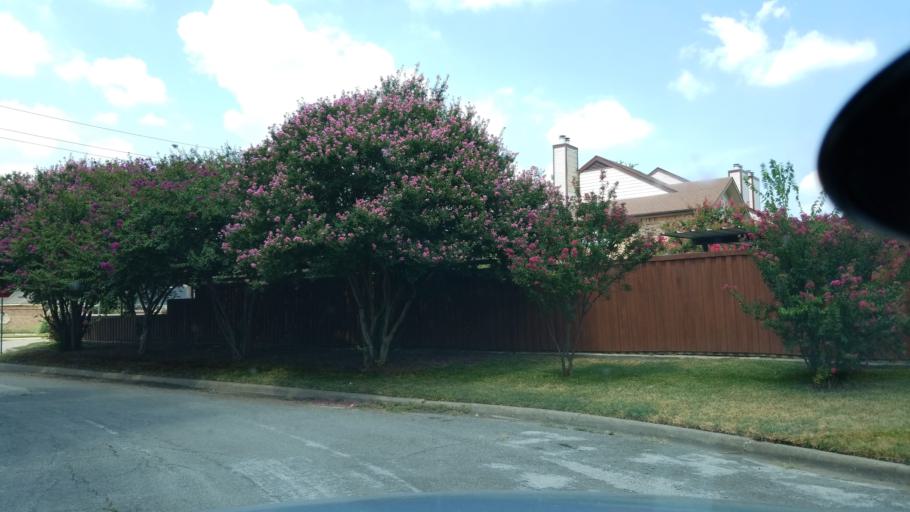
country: US
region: Texas
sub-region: Dallas County
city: Richardson
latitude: 32.9293
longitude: -96.7175
